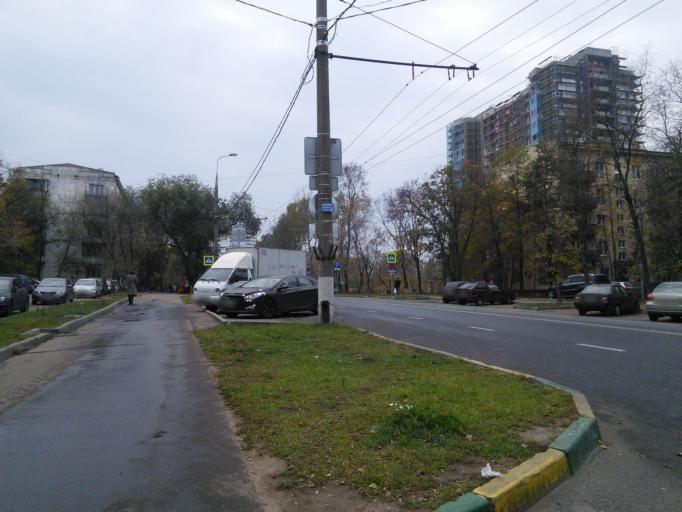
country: RU
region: Moskovskaya
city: Khoroshevo-Mnevniki
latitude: 55.7820
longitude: 37.4623
